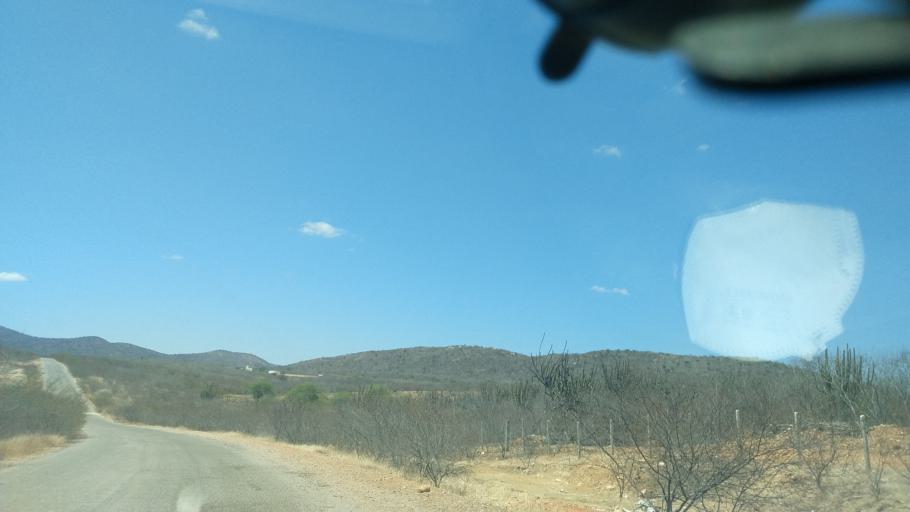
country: BR
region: Rio Grande do Norte
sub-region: Sao Tome
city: Sao Tome
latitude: -5.9695
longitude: -36.1319
